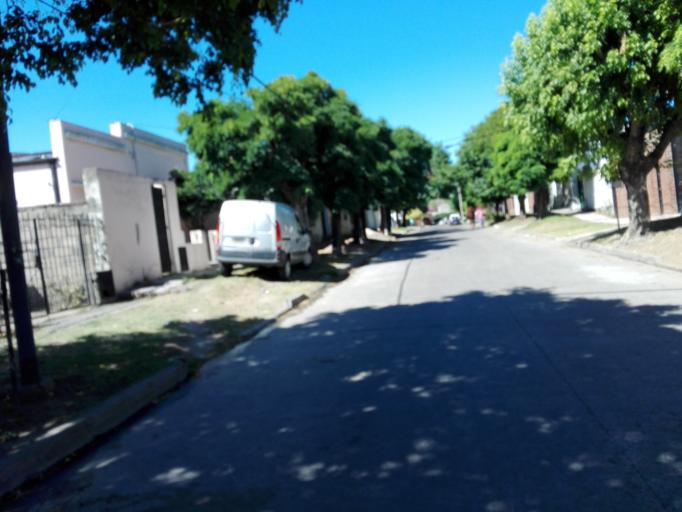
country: AR
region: Buenos Aires
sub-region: Partido de La Plata
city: La Plata
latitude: -34.8956
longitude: -57.9437
